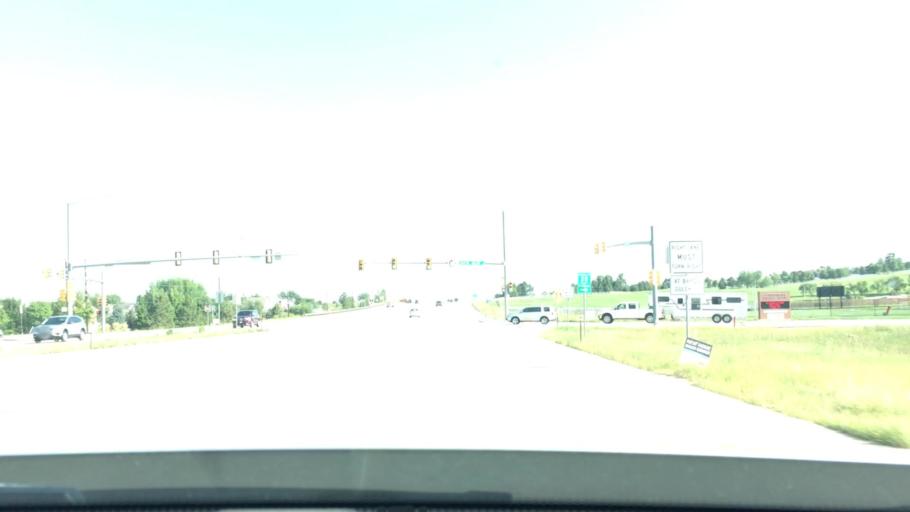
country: US
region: Colorado
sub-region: Douglas County
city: The Pinery
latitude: 39.4343
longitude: -104.7601
